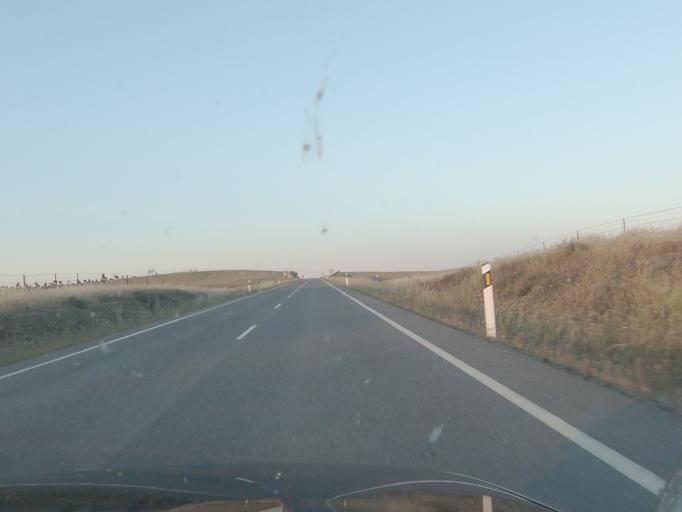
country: ES
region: Extremadura
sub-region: Provincia de Caceres
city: Alcantara
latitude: 39.6102
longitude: -6.9616
